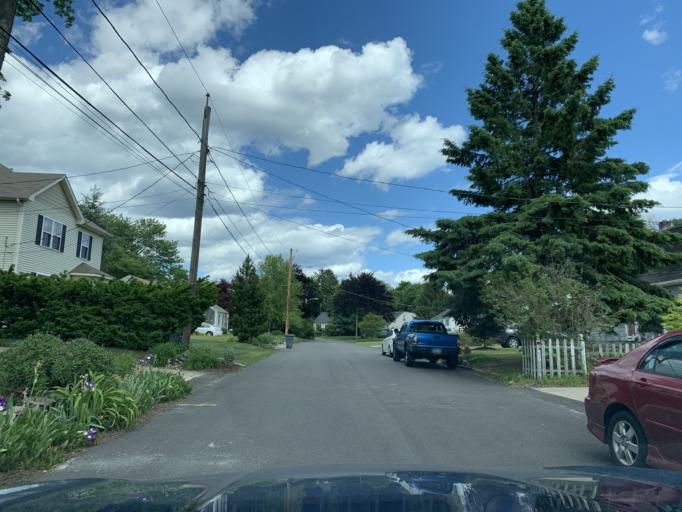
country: US
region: Rhode Island
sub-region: Kent County
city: East Greenwich
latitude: 41.6215
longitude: -71.4611
